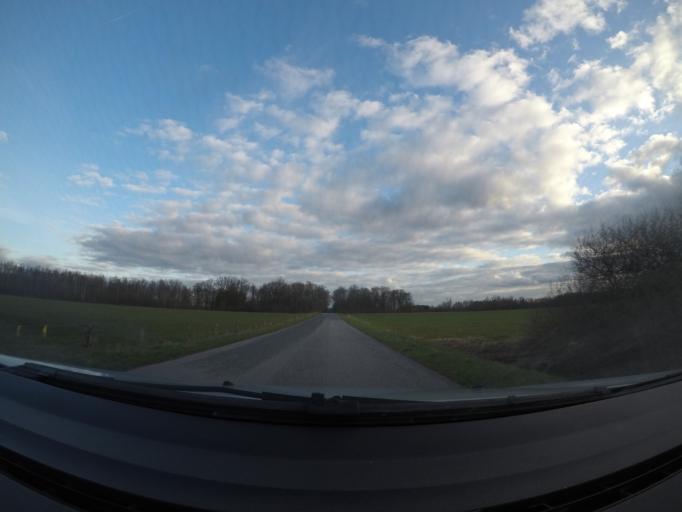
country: BE
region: Wallonia
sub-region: Province du Luxembourg
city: Etalle
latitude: 49.6912
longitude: 5.5617
